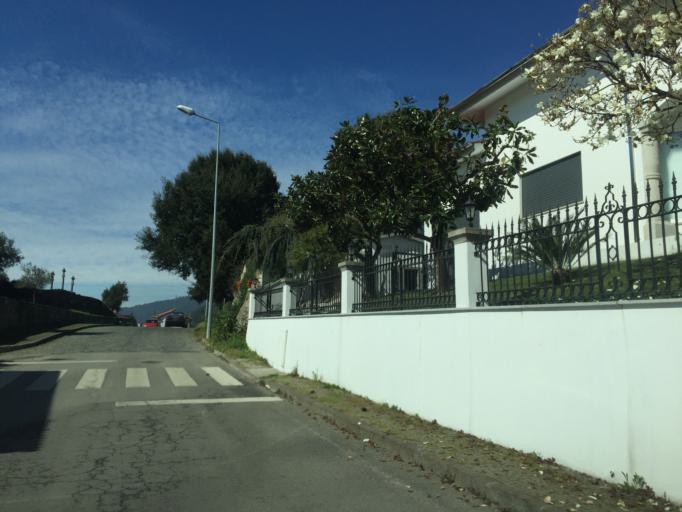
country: PT
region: Aveiro
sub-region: Arouca
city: Arouca
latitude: 40.9325
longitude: -8.2465
